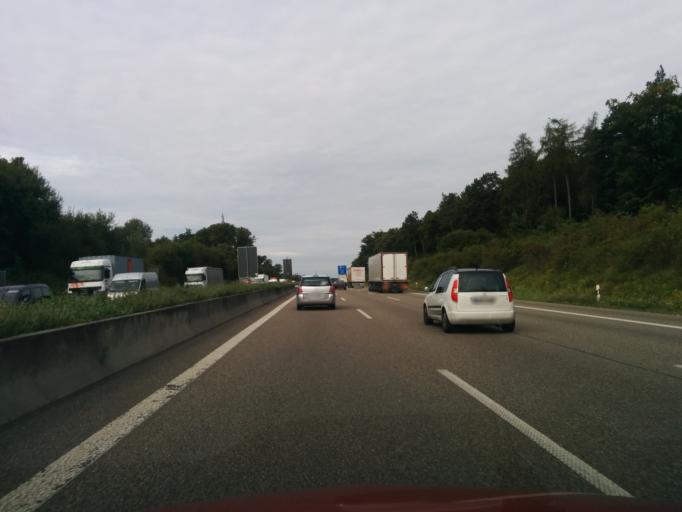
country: DE
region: Baden-Wuerttemberg
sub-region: Karlsruhe Region
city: Ispringen
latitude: 48.9079
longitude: 8.6711
